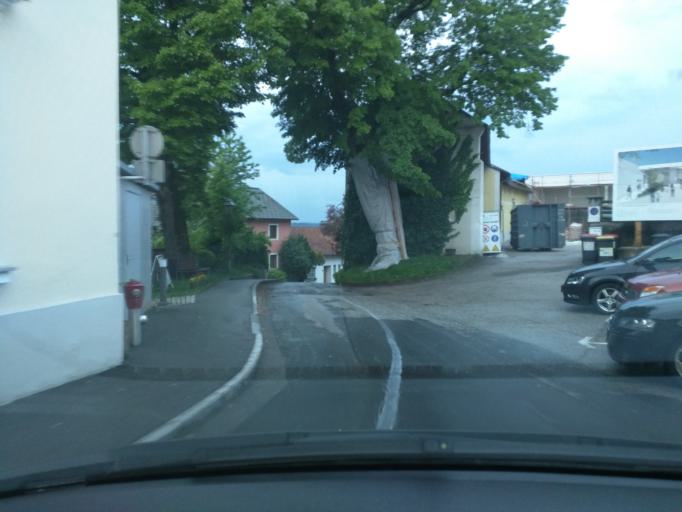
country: AT
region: Lower Austria
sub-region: Politischer Bezirk Amstetten
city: Sankt Georgen am Ybbsfelde
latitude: 48.1294
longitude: 14.9543
